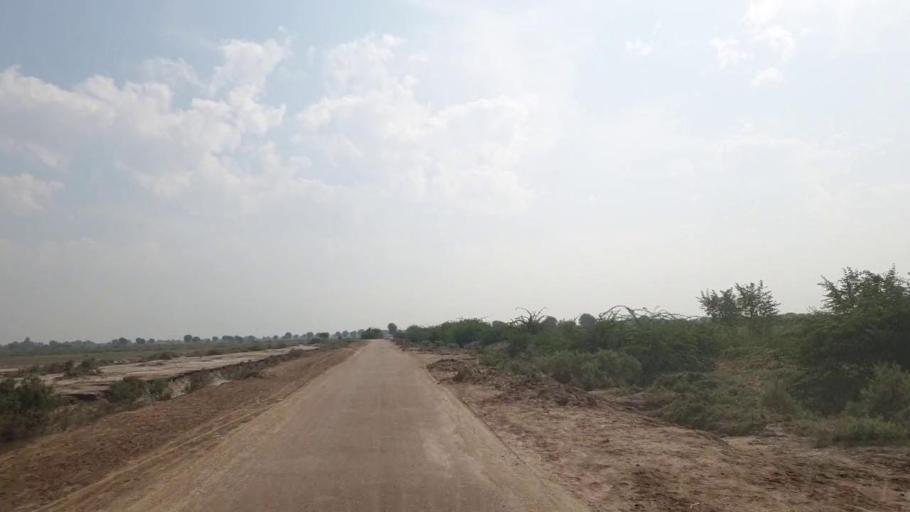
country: PK
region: Sindh
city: Rajo Khanani
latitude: 24.9659
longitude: 69.0109
